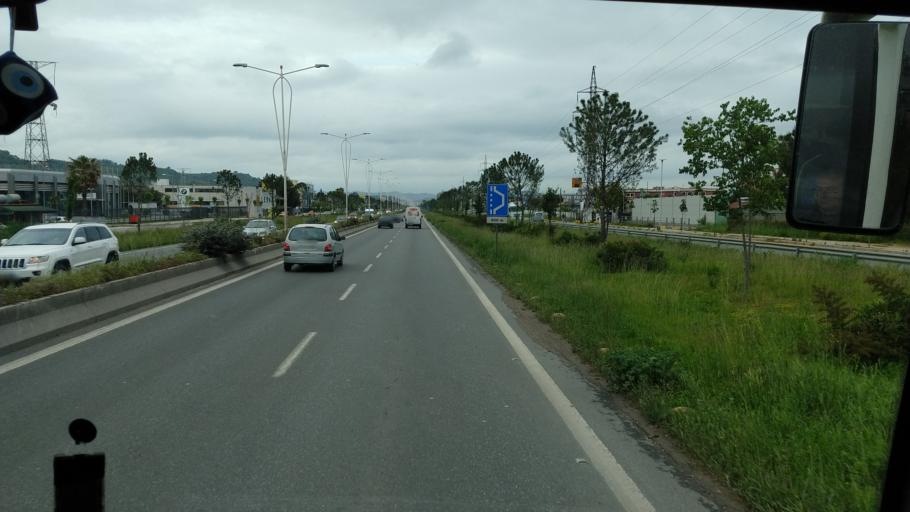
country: AL
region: Tirane
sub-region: Rrethi i Tiranes
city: Kamez
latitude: 41.3481
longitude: 19.7614
